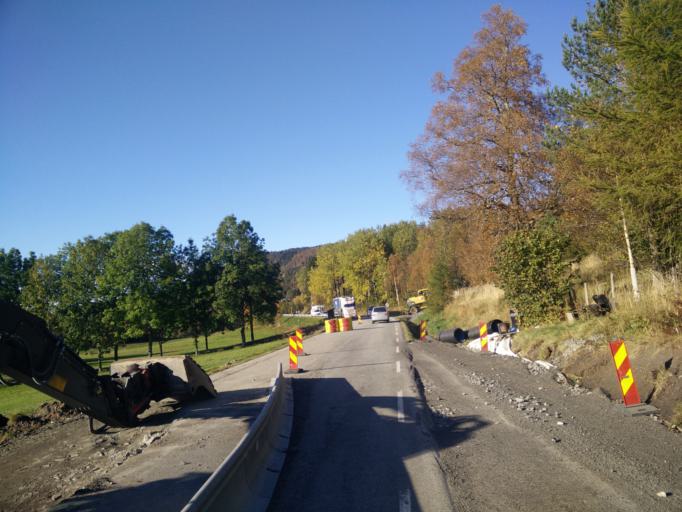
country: NO
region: More og Romsdal
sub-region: Halsa
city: Liaboen
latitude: 63.1123
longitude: 8.3258
